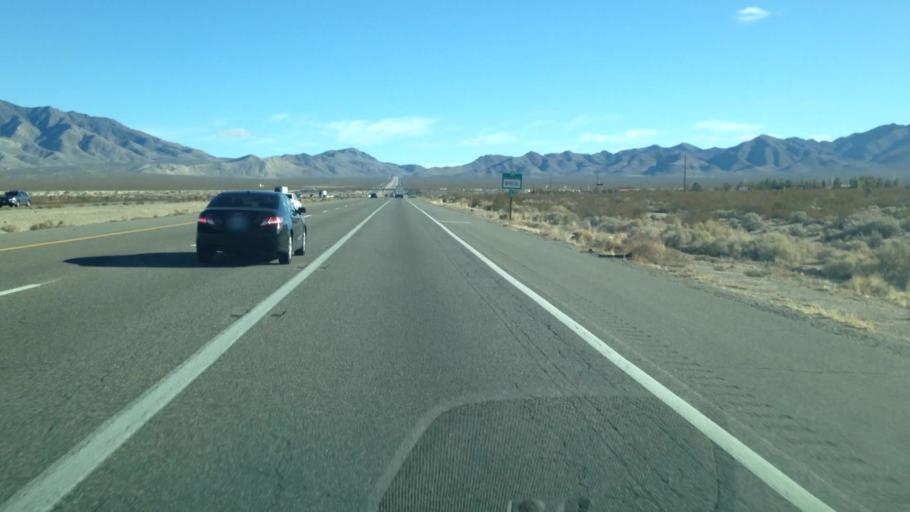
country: US
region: Nevada
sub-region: Clark County
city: Sandy Valley
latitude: 35.4391
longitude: -115.6876
